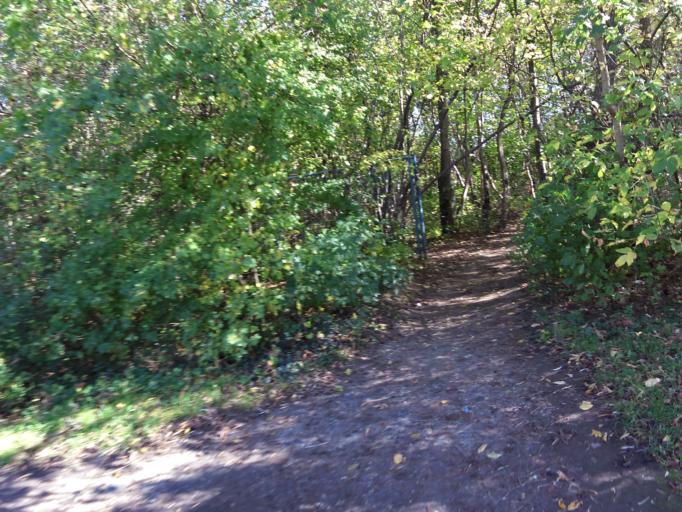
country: DE
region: Saxony
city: Leipzig
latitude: 51.3802
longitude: 12.3654
